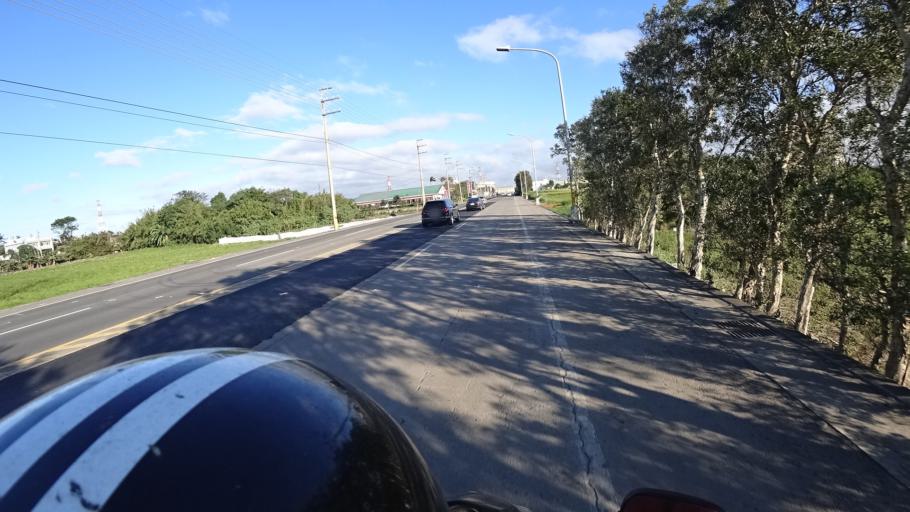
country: TW
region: Taiwan
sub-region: Hsinchu
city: Zhubei
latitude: 24.9823
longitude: 121.0620
